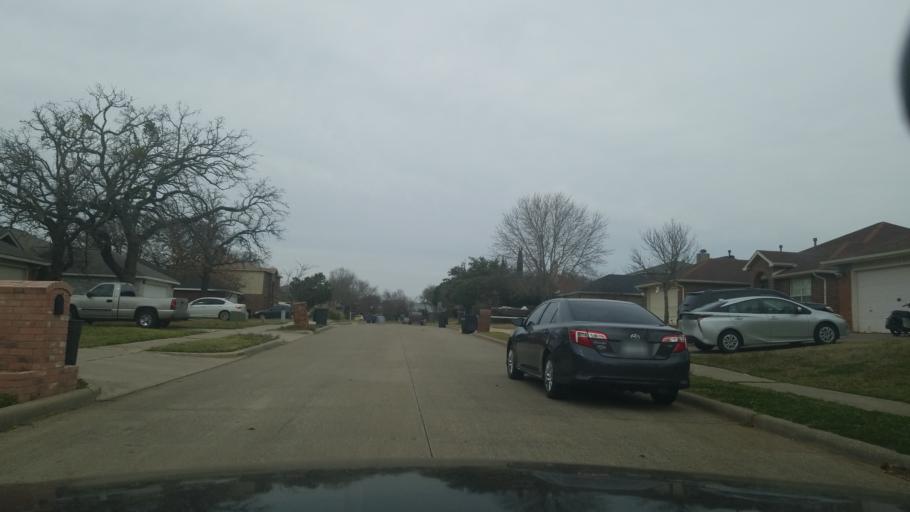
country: US
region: Texas
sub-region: Denton County
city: Hickory Creek
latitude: 33.1309
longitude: -97.0595
